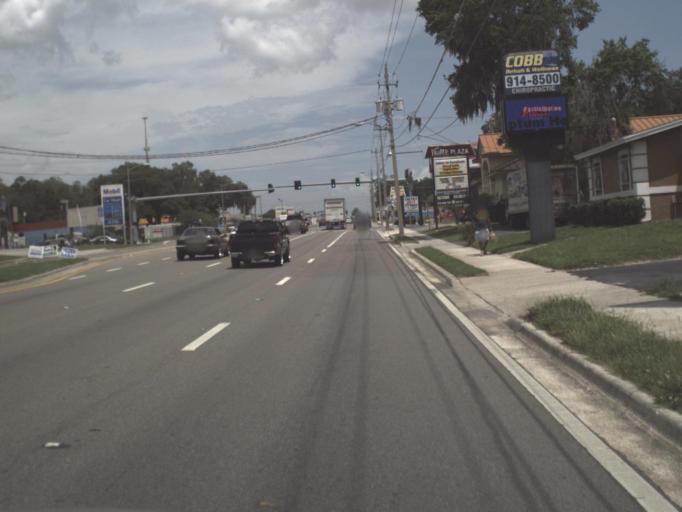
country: US
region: Florida
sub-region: Hillsborough County
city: Temple Terrace
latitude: 28.0325
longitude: -82.4113
